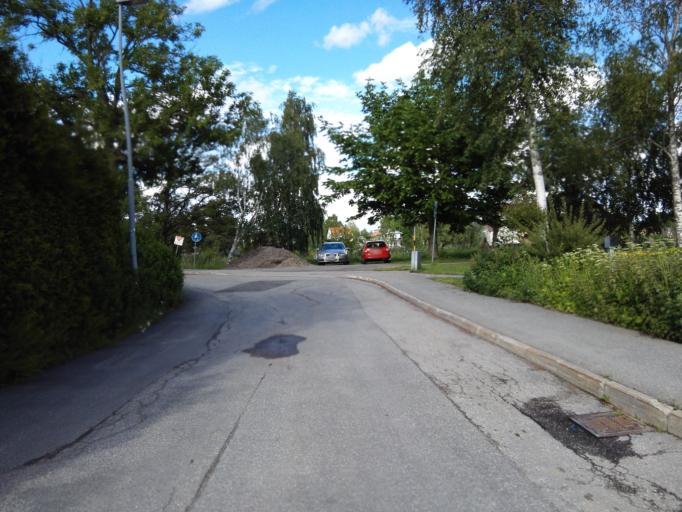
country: SE
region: Stockholm
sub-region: Huddinge Kommun
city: Segeltorp
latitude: 59.2690
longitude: 17.9595
